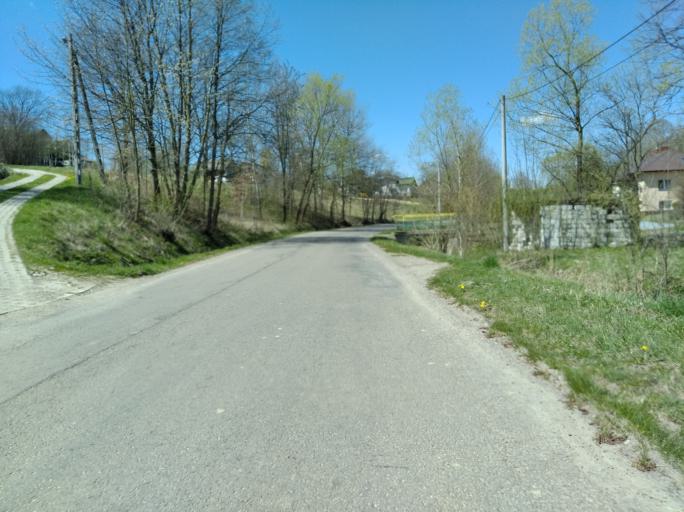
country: PL
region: Subcarpathian Voivodeship
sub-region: Powiat brzozowski
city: Jablonka
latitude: 49.7189
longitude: 22.1243
